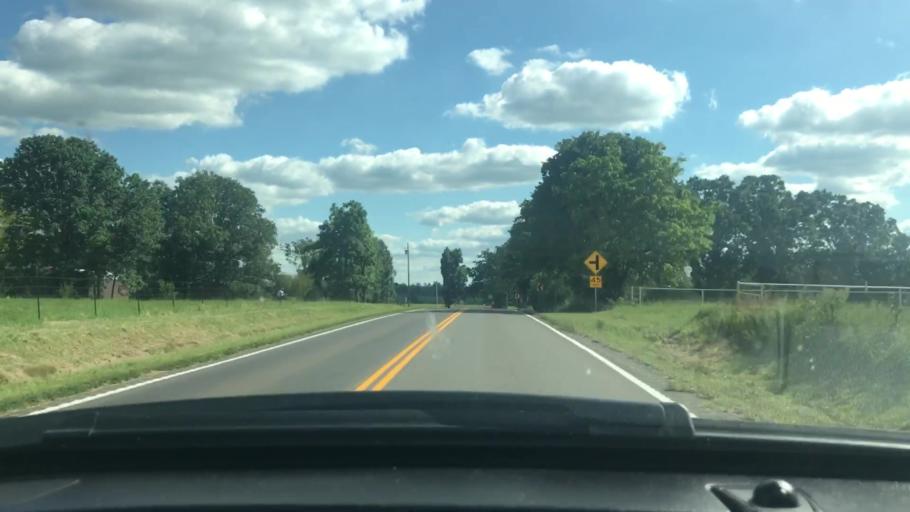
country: US
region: Missouri
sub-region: Wright County
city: Mountain Grove
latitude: 37.2580
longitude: -92.3082
